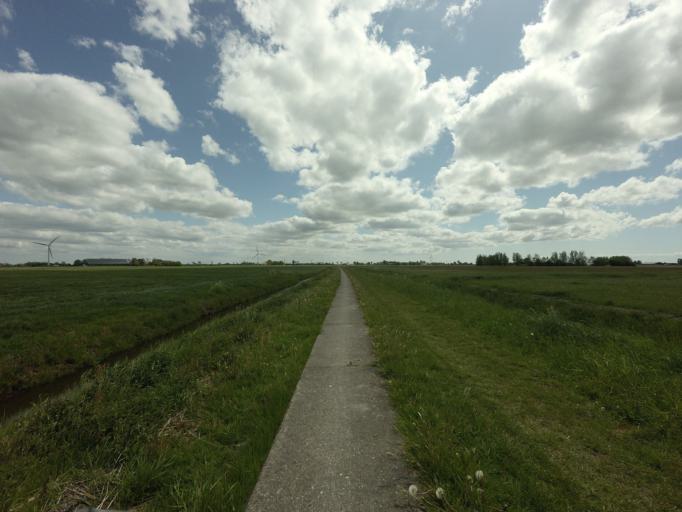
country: NL
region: Friesland
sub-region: Gemeente Franekeradeel
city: Tzum
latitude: 53.1341
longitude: 5.5733
